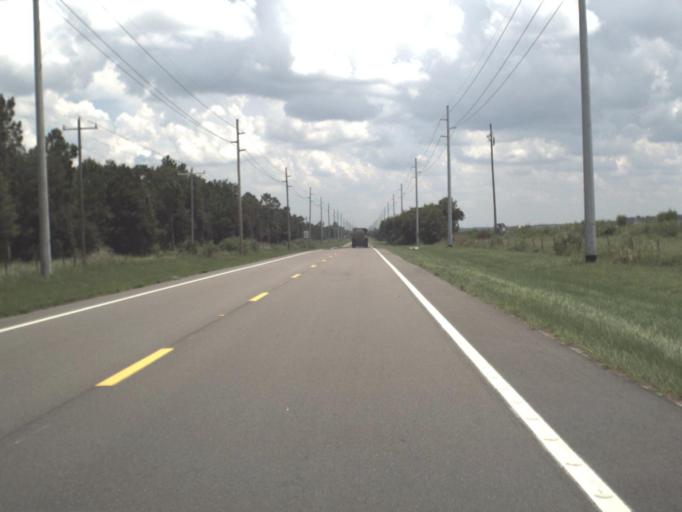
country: US
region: Florida
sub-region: Hillsborough County
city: Balm
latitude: 27.7045
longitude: -82.1370
